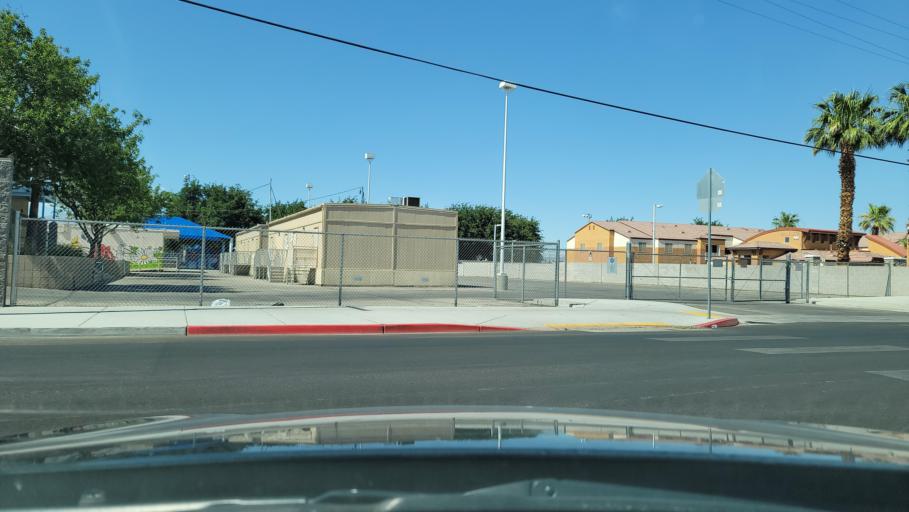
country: US
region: Nevada
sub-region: Clark County
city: Las Vegas
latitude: 36.1920
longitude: -115.1544
